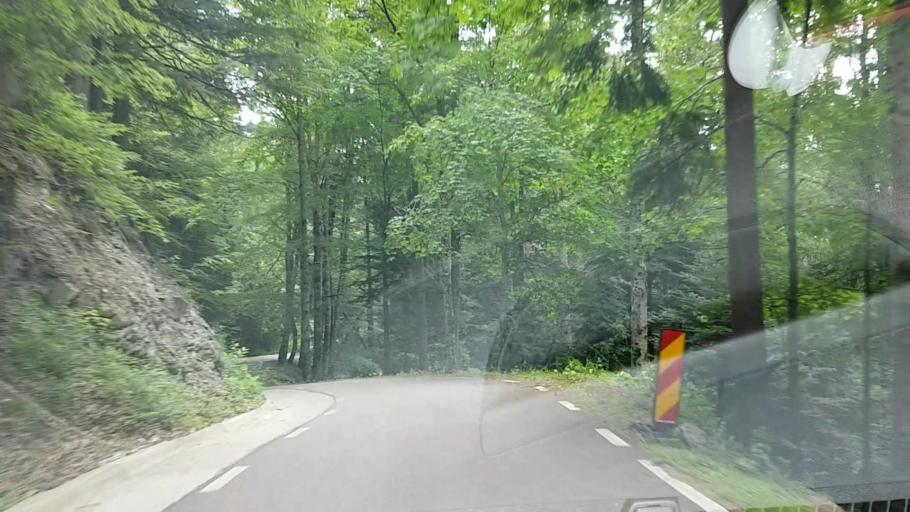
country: RO
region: Suceava
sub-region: Comuna Crucea
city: Crucea
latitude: 47.4339
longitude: 25.5736
